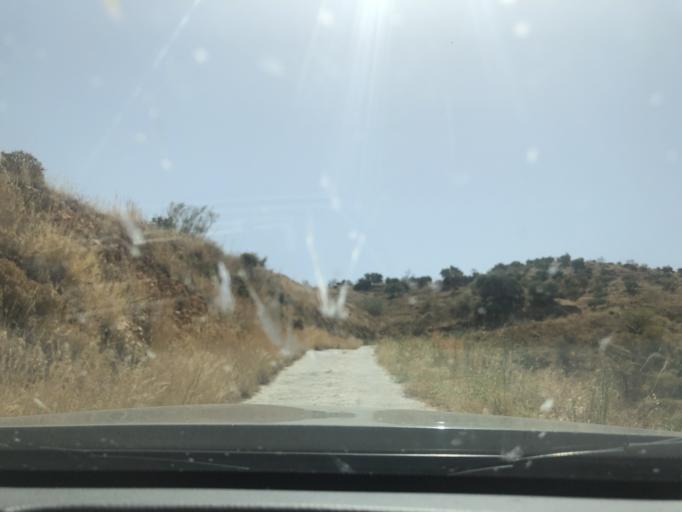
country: ES
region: Andalusia
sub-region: Provincia de Malaga
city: Cartama
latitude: 36.7088
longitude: -4.6257
